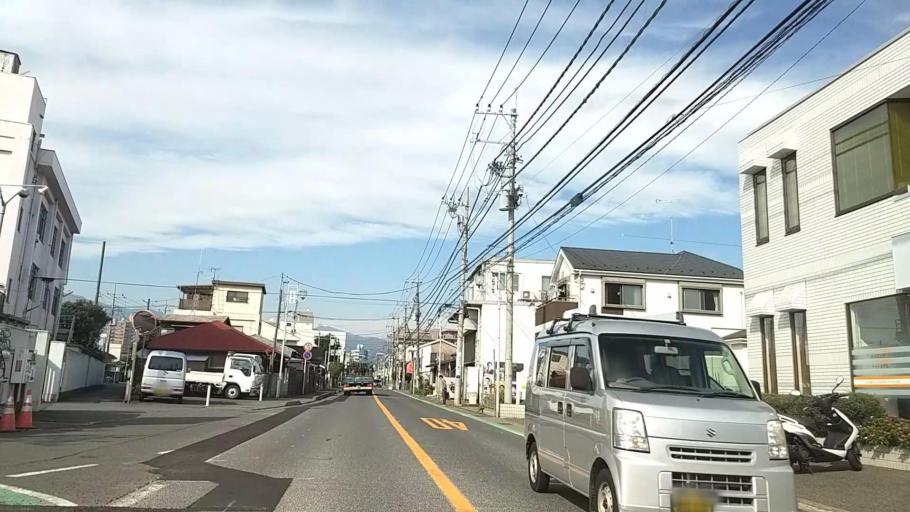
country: JP
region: Kanagawa
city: Atsugi
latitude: 35.4473
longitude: 139.3654
